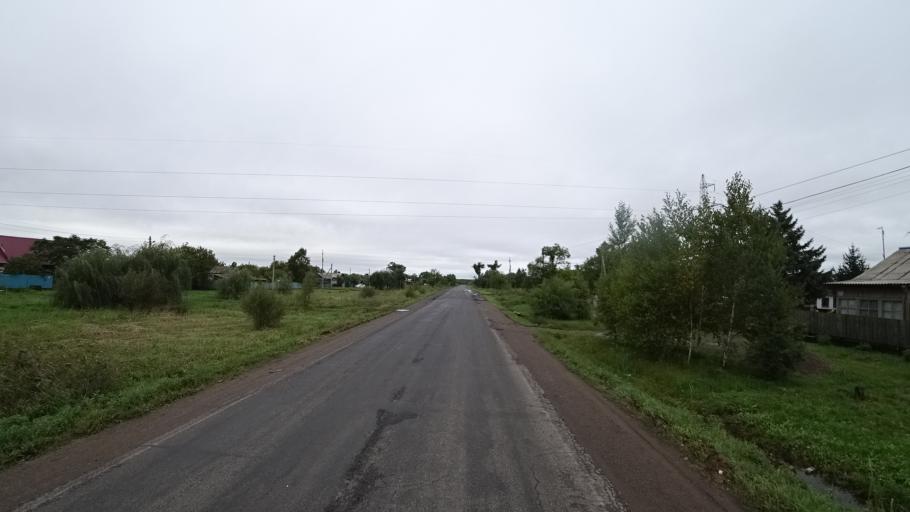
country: RU
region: Primorskiy
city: Monastyrishche
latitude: 44.2001
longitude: 132.4767
